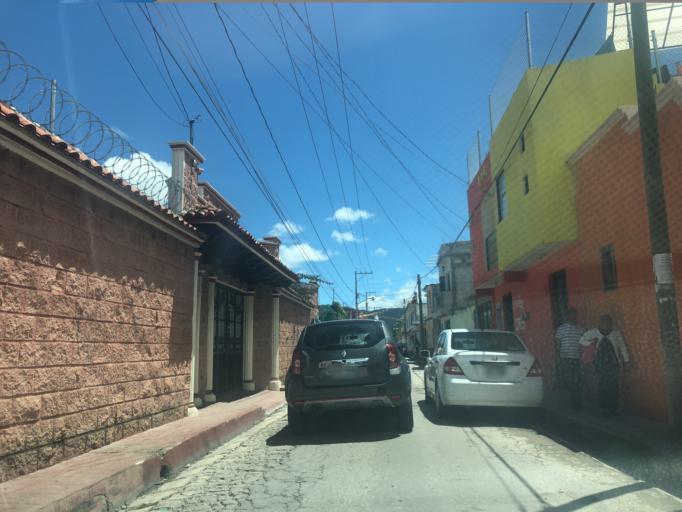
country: MX
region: Chiapas
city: San Cristobal de las Casas
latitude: 16.7175
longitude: -92.6430
